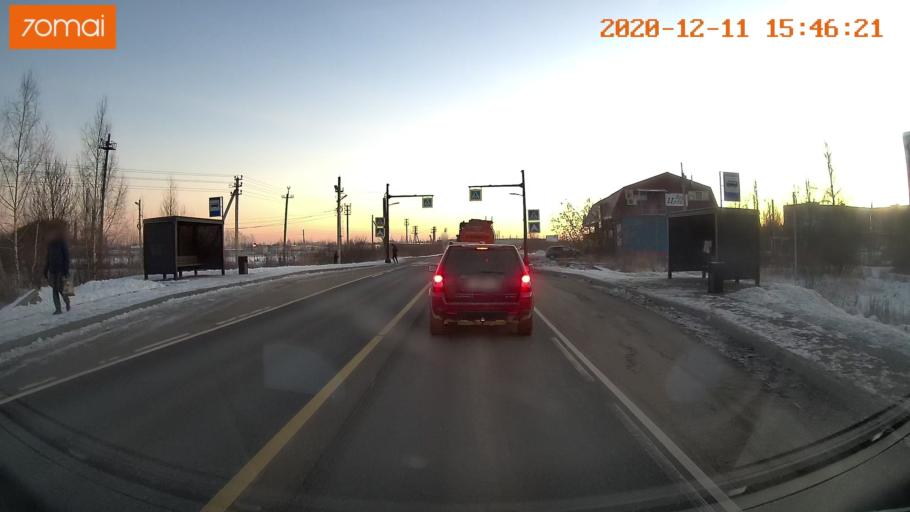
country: RU
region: Ivanovo
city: Novo-Talitsy
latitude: 57.0057
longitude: 40.8547
